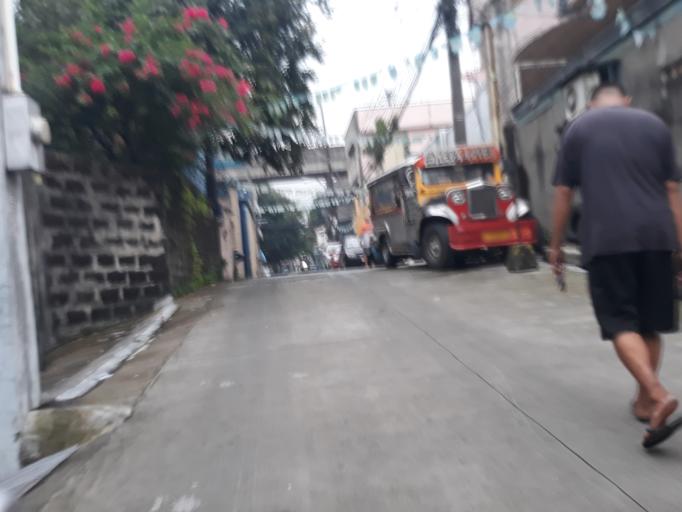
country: PH
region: Metro Manila
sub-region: San Juan
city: San Juan
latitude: 14.6117
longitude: 121.0272
